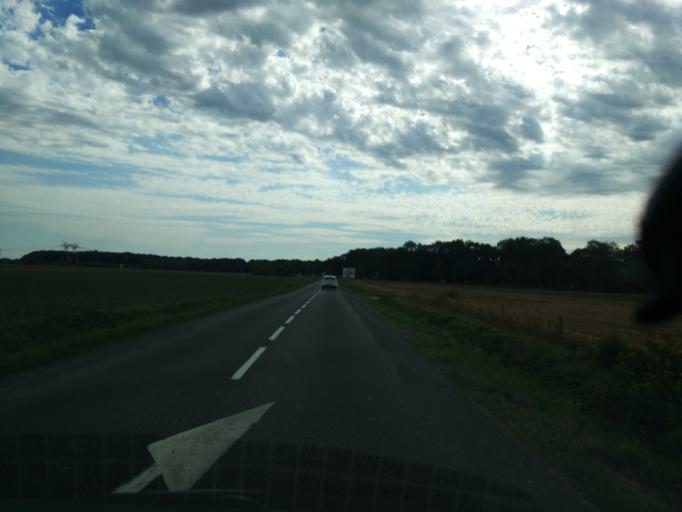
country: FR
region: Ile-de-France
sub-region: Departement de l'Essonne
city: Briis-sous-Forges
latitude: 48.6436
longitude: 2.1214
